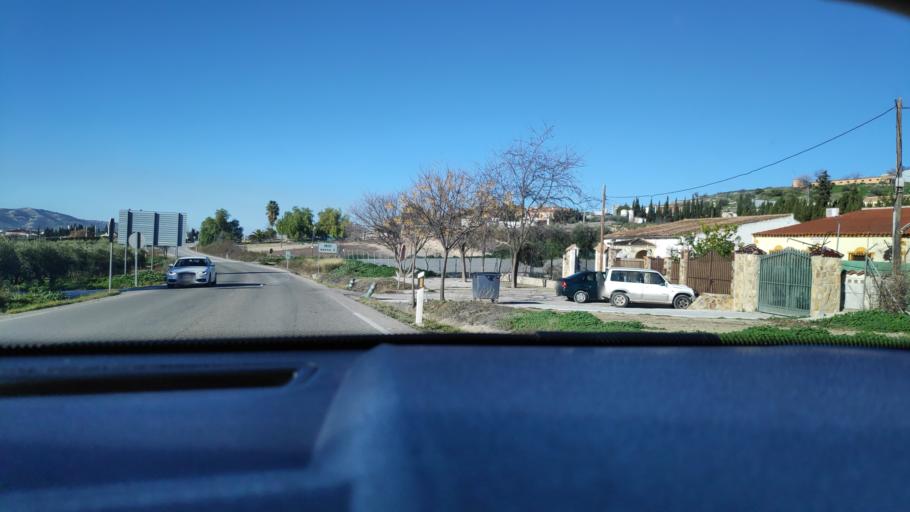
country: ES
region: Andalusia
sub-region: Province of Cordoba
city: Baena
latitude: 37.6232
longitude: -4.3016
